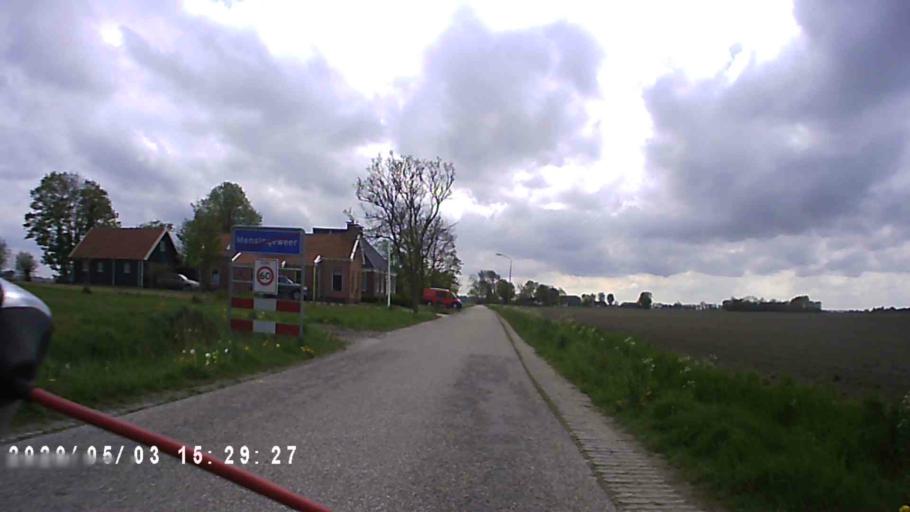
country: NL
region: Groningen
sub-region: Gemeente Winsum
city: Winsum
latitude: 53.3493
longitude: 6.4632
